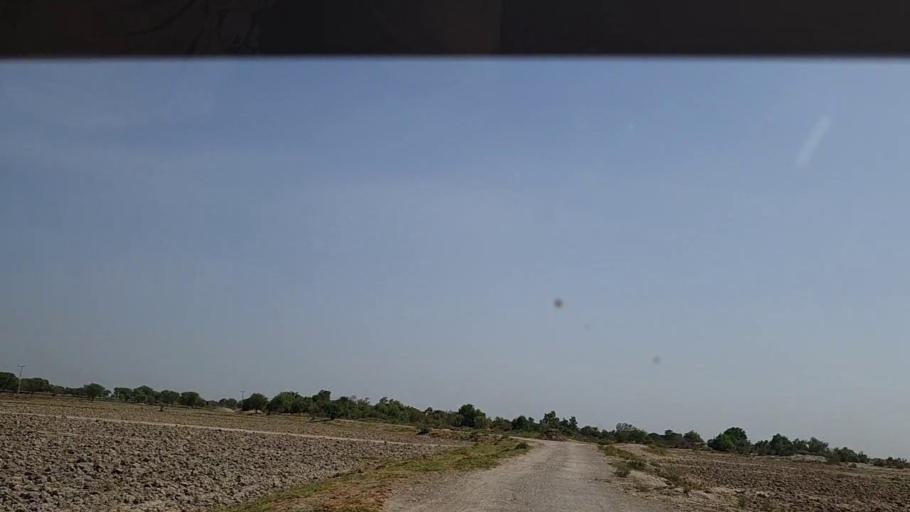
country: PK
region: Sindh
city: Phulji
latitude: 26.9483
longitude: 67.7160
